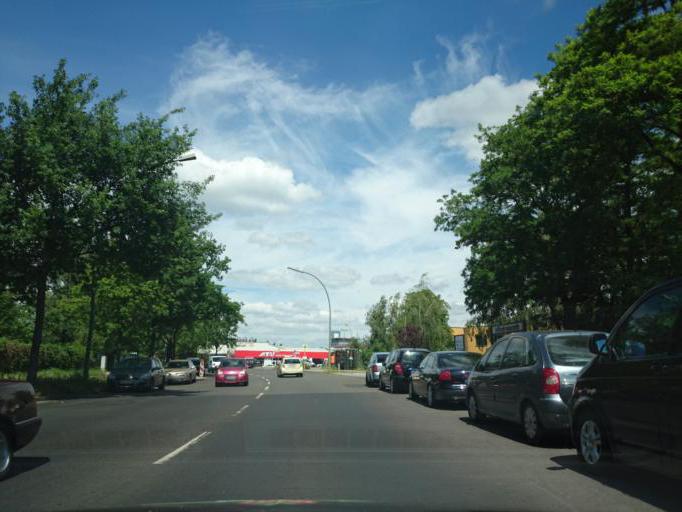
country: DE
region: Berlin
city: Marienfelde
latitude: 52.4034
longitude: 13.3828
